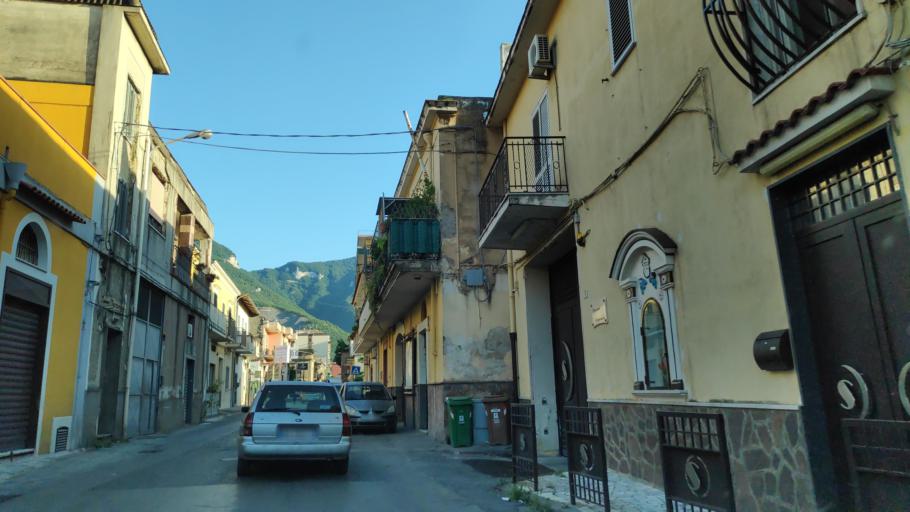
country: IT
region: Campania
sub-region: Provincia di Salerno
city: Pagani
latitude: 40.7504
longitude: 14.6150
